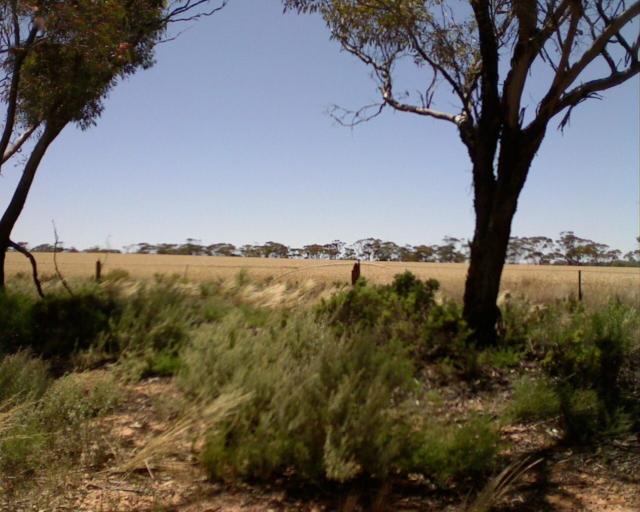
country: AU
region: South Australia
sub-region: Kimba
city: Caralue
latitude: -32.9478
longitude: 135.2754
